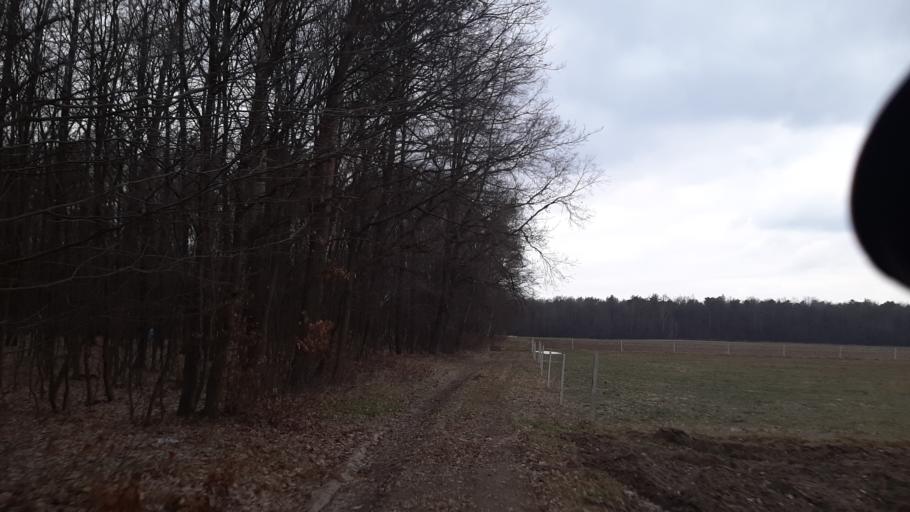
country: PL
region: Lublin Voivodeship
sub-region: Powiat lubelski
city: Garbow
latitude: 51.3910
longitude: 22.4015
